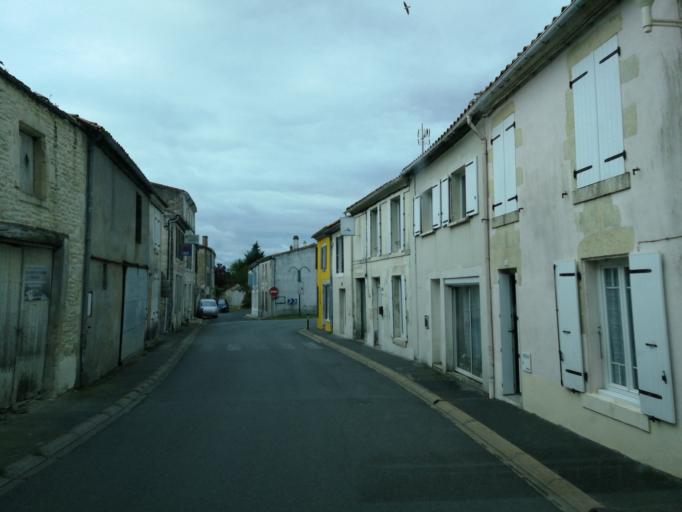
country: FR
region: Pays de la Loire
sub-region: Departement de la Vendee
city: Vix
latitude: 46.3729
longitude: -0.9229
